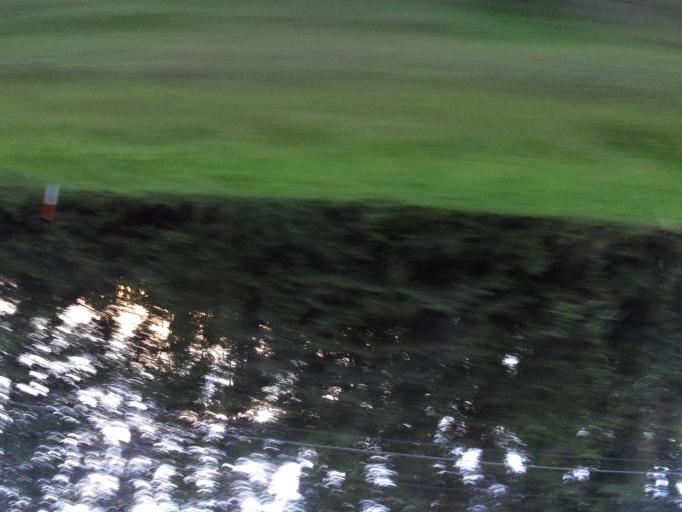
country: US
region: Georgia
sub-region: Camden County
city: Woodbine
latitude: 30.9240
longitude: -81.7148
